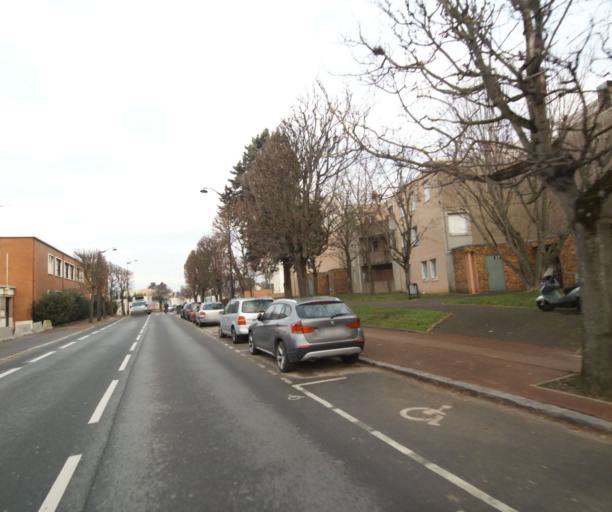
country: FR
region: Ile-de-France
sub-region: Departement des Hauts-de-Seine
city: Rueil-Malmaison
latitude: 48.8737
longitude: 2.2015
